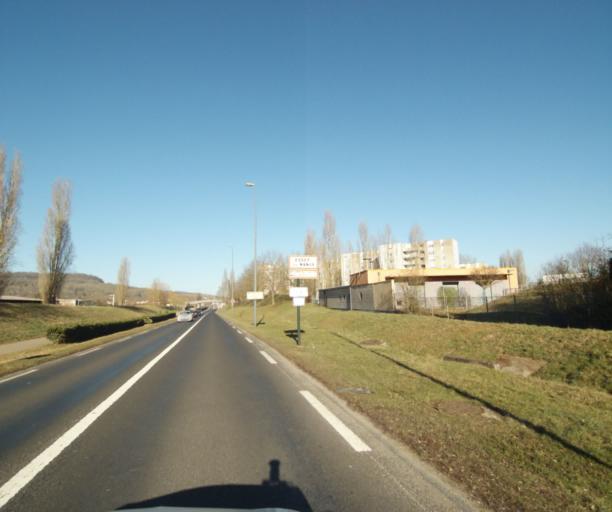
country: FR
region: Lorraine
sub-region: Departement de Meurthe-et-Moselle
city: Essey-les-Nancy
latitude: 48.6971
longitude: 6.2207
